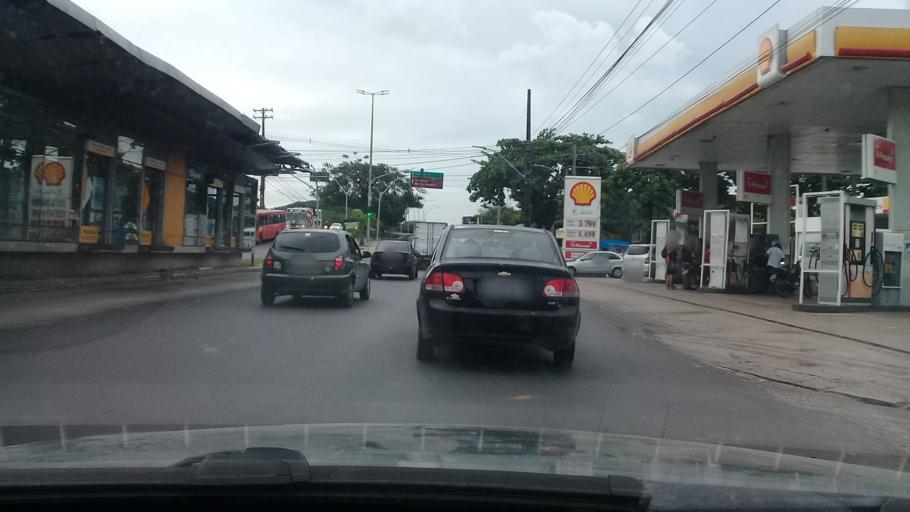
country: BR
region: Pernambuco
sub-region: Sao Lourenco Da Mata
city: Sao Lourenco da Mata
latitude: -8.0315
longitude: -34.9552
